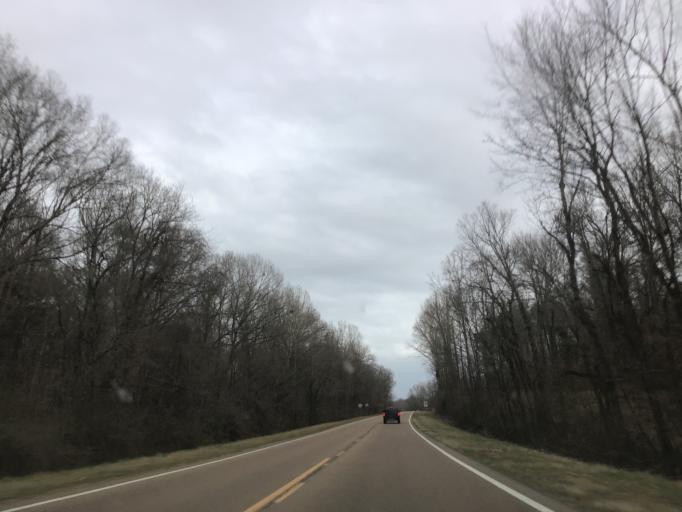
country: US
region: Mississippi
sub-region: Warren County
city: Beechwood
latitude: 32.3160
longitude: -90.8109
